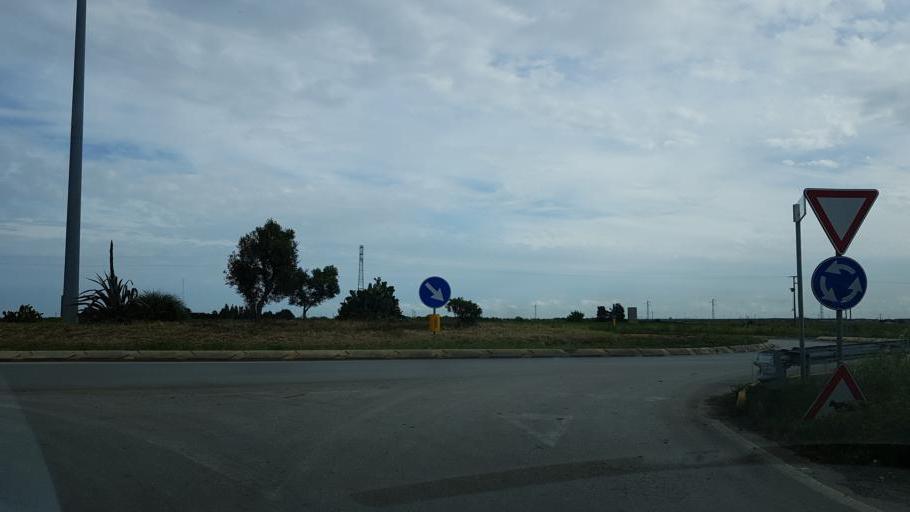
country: IT
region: Apulia
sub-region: Provincia di Brindisi
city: Brindisi
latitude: 40.6485
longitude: 17.8632
